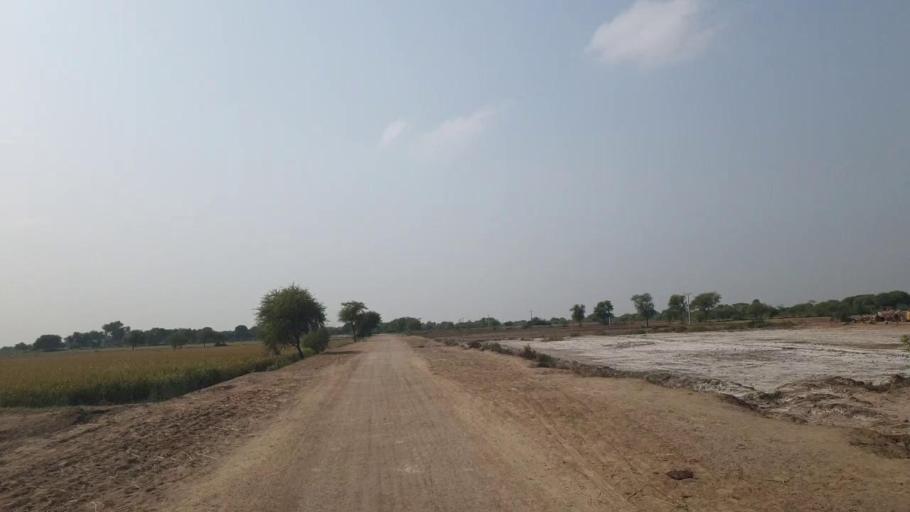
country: PK
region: Sindh
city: Badin
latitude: 24.5468
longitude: 68.6629
